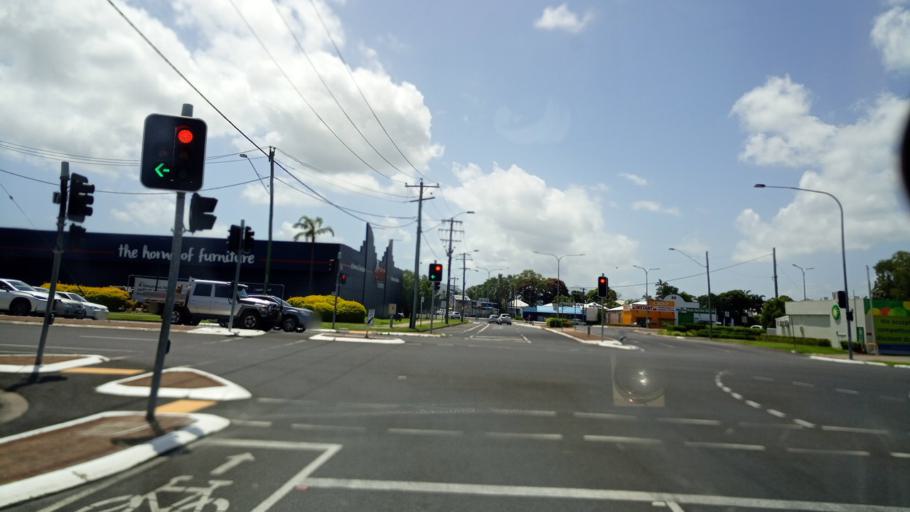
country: AU
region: Queensland
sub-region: Cairns
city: Cairns
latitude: -16.9228
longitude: 145.7674
